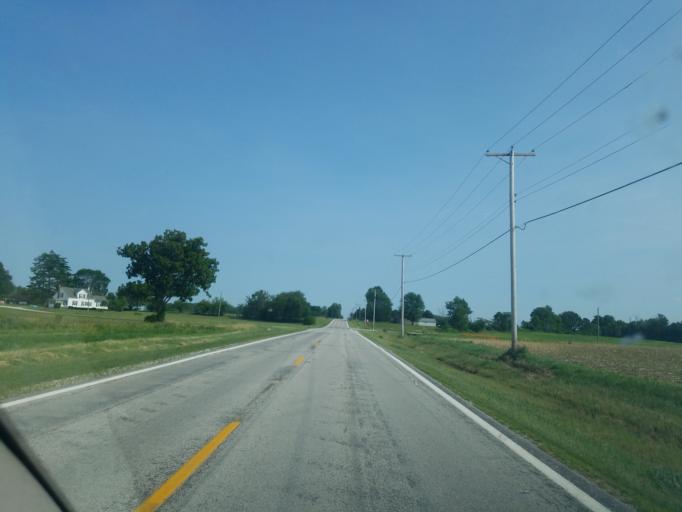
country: US
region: Ohio
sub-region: Wyandot County
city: Carey
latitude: 41.0375
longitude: -83.3059
